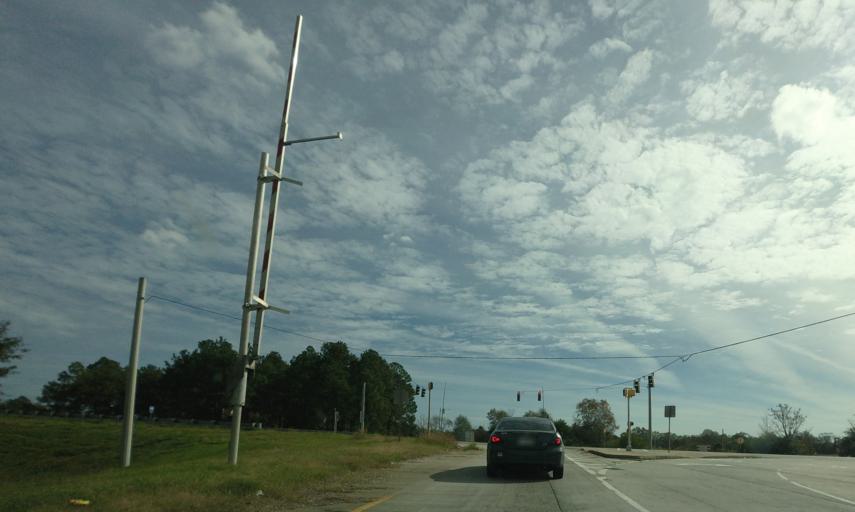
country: US
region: Georgia
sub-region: Laurens County
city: Dublin
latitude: 32.4966
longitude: -82.9802
